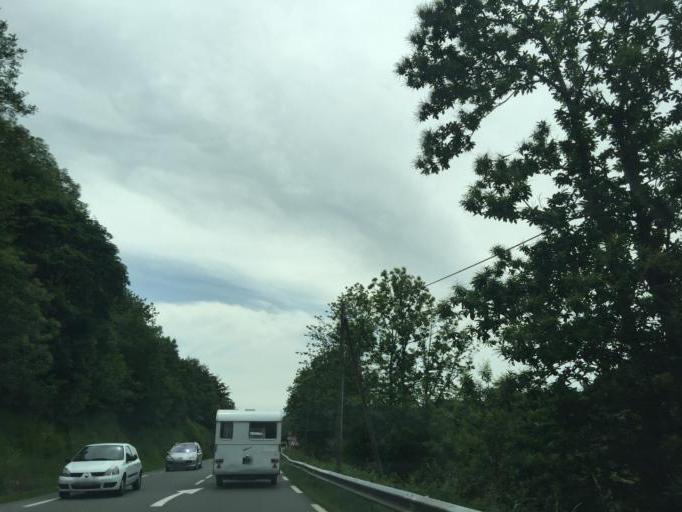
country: FR
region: Rhone-Alpes
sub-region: Departement de la Loire
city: Bourg-Argental
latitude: 45.3170
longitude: 4.5235
